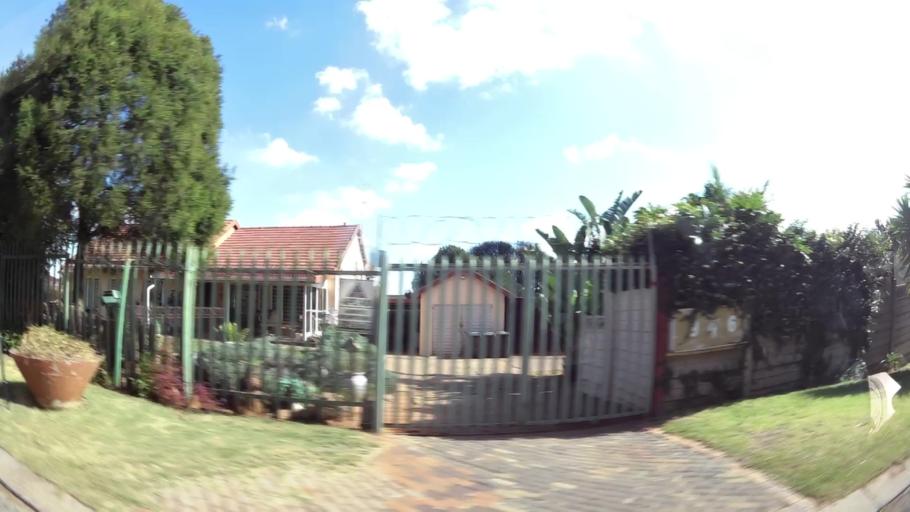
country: ZA
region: Gauteng
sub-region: City of Johannesburg Metropolitan Municipality
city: Roodepoort
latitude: -26.1284
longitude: 27.8391
